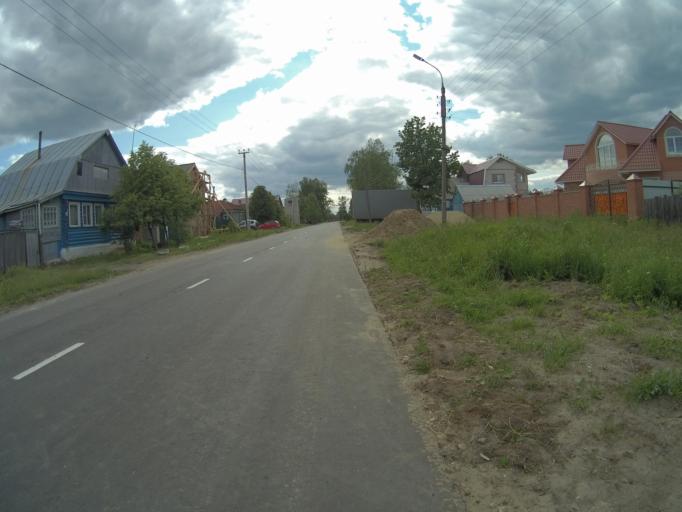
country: RU
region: Vladimir
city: Sudogda
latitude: 55.9526
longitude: 40.8538
